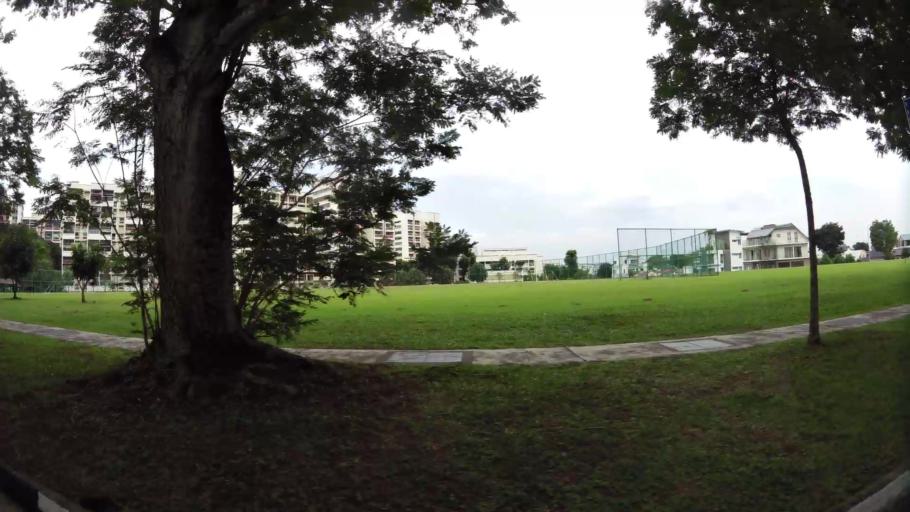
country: SG
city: Singapore
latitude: 1.3643
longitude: 103.8729
